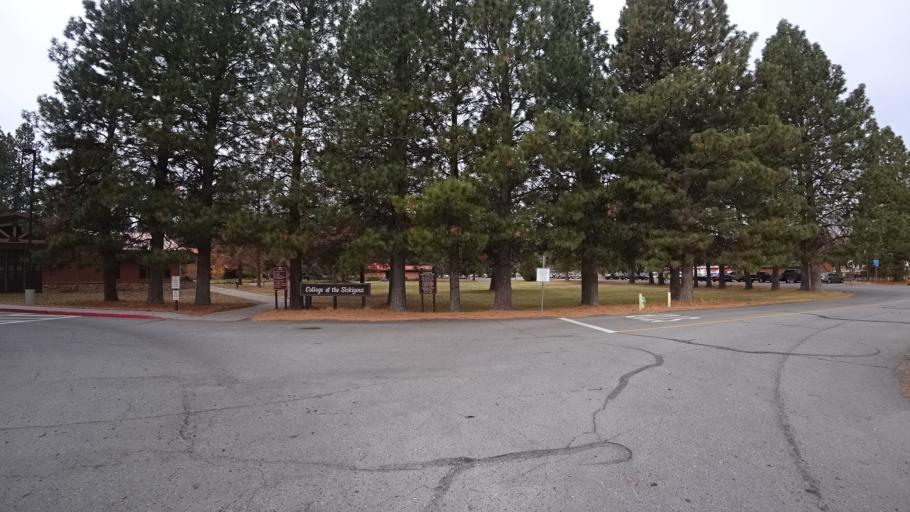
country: US
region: California
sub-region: Siskiyou County
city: Weed
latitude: 41.4142
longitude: -122.3869
